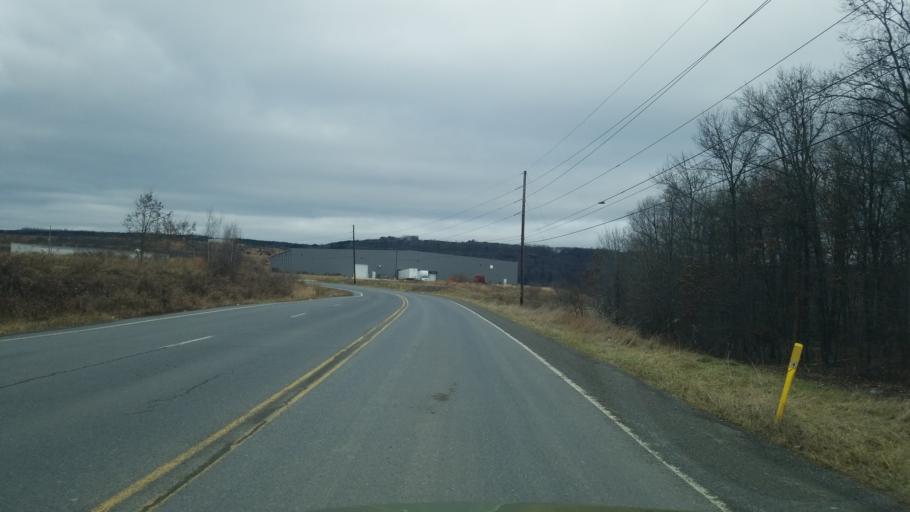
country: US
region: Pennsylvania
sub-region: Clearfield County
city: Clearfield
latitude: 41.0296
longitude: -78.3885
